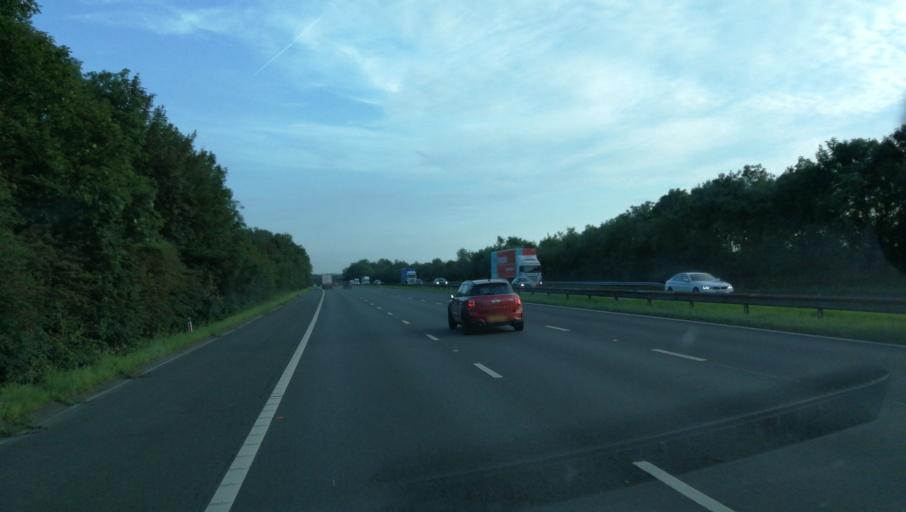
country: GB
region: England
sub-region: Cumbria
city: Milnthorpe
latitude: 54.2043
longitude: -2.7239
